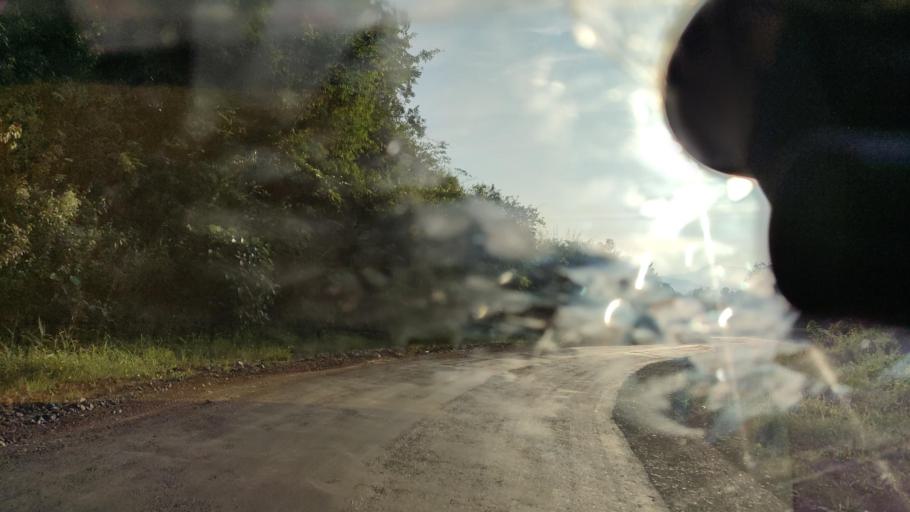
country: MM
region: Magway
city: Minbu
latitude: 19.8549
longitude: 94.1272
